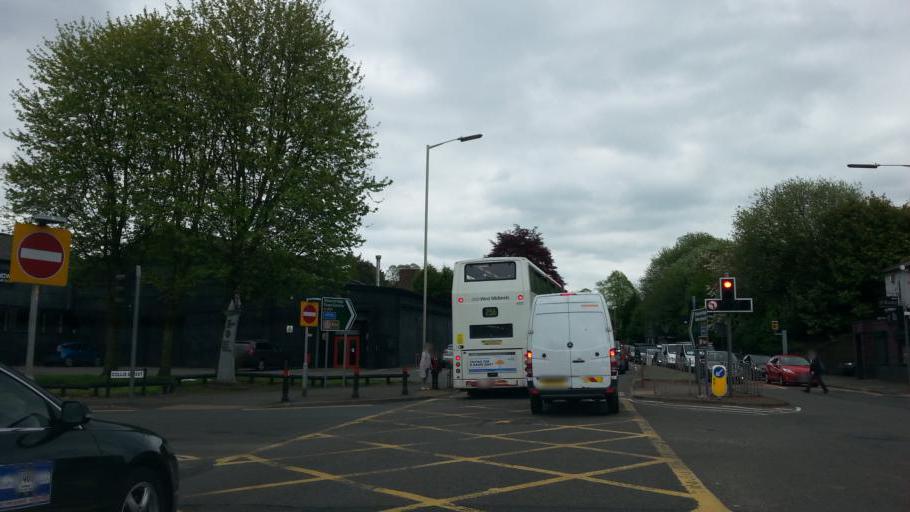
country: GB
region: England
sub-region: Dudley
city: Stourbridge
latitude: 52.4682
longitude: -2.1532
